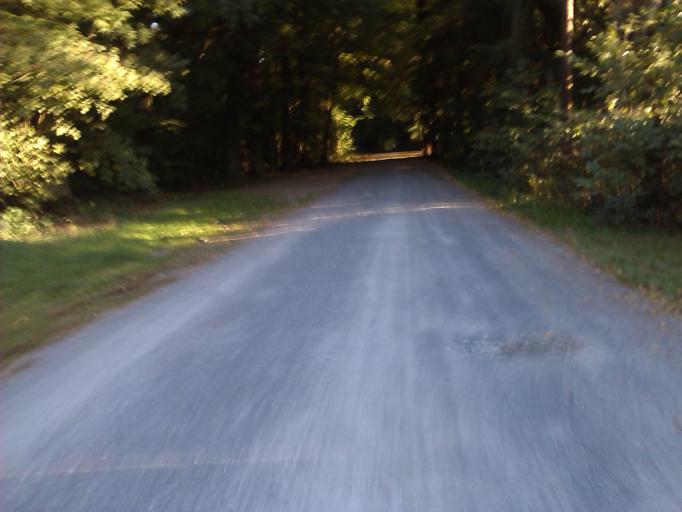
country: DE
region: Hesse
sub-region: Regierungsbezirk Darmstadt
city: Erzhausen
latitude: 49.9692
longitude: 8.6323
